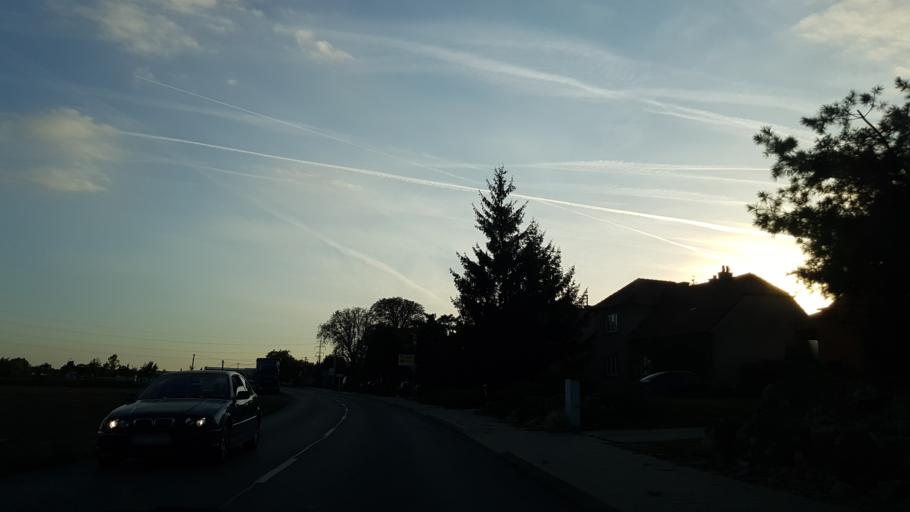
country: CZ
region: Zlin
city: Polesovice
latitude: 49.0259
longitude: 17.3564
